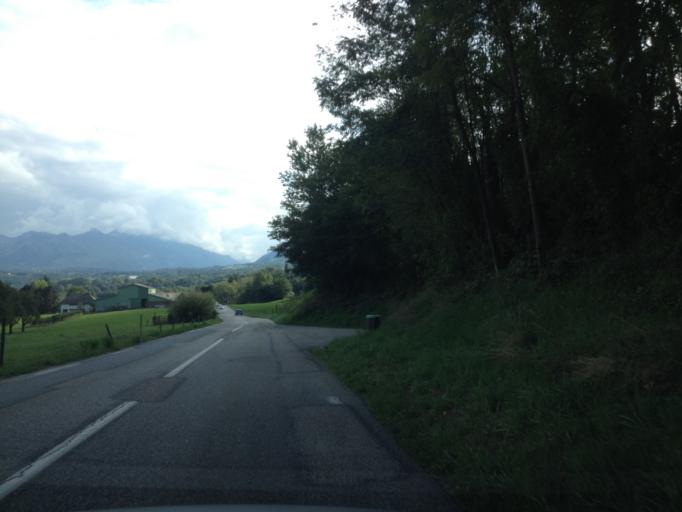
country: FR
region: Rhone-Alpes
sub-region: Departement de la Savoie
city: La Motte-Servolex
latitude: 45.6146
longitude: 5.8607
